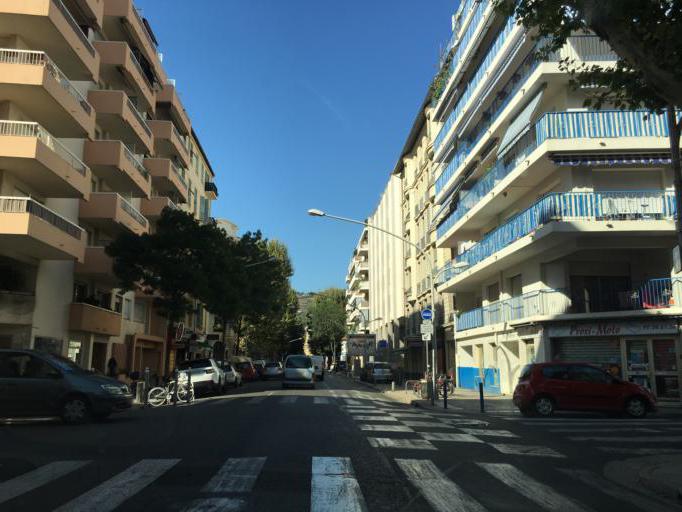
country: FR
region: Provence-Alpes-Cote d'Azur
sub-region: Departement des Alpes-Maritimes
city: Villefranche-sur-Mer
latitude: 43.7019
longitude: 7.2886
